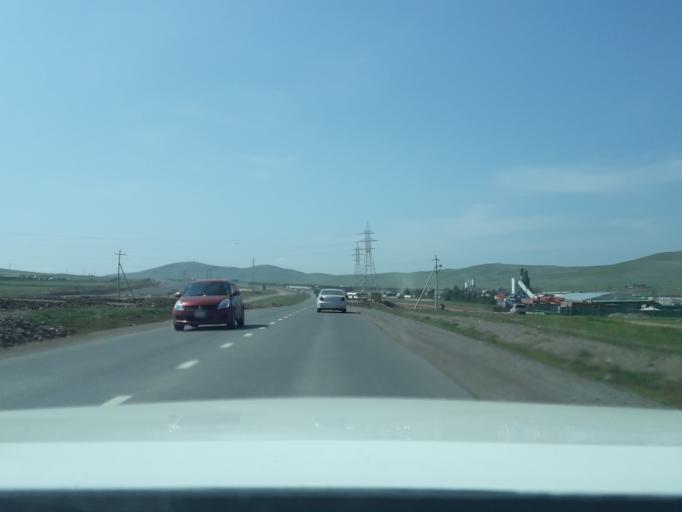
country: MN
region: Ulaanbaatar
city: Ulaanbaatar
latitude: 47.8211
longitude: 106.7615
